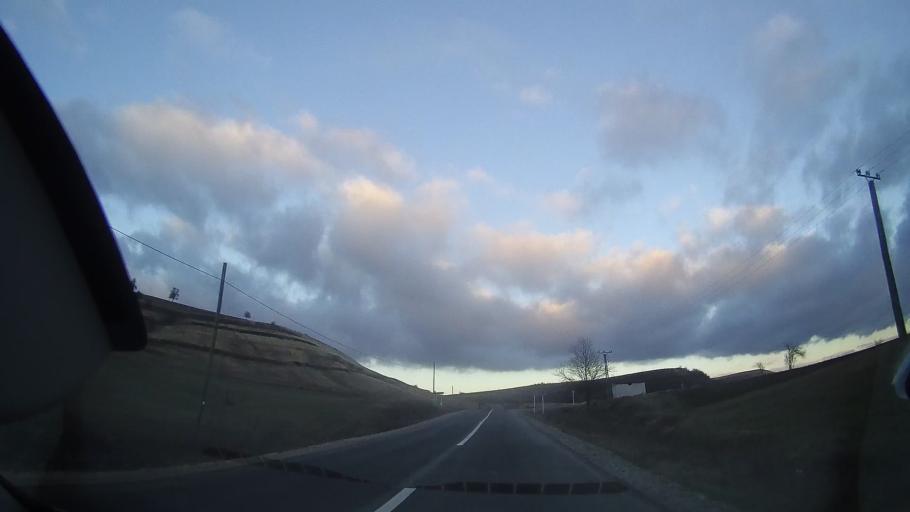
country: RO
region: Cluj
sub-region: Comuna Izvoru Crisului
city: Izvoru Crisului
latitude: 46.8076
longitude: 23.1173
